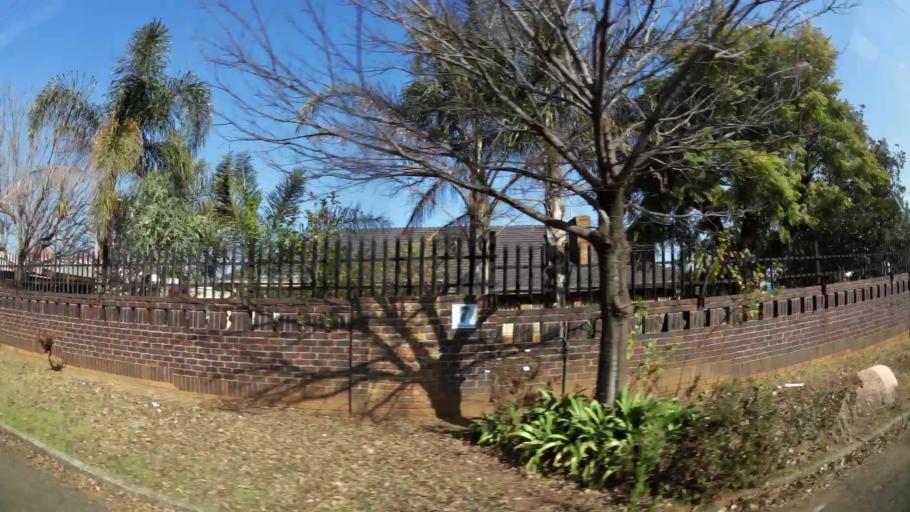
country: ZA
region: Gauteng
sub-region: West Rand District Municipality
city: Randfontein
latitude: -26.1624
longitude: 27.7003
